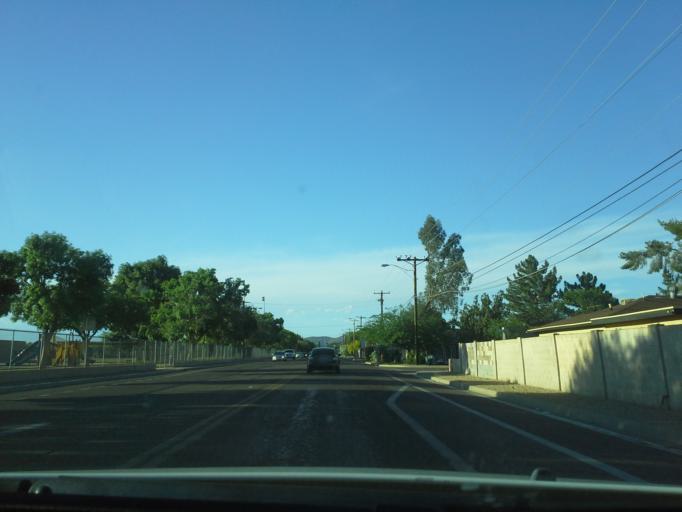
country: US
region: Arizona
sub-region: Maricopa County
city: Phoenix
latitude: 33.5171
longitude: -112.0912
